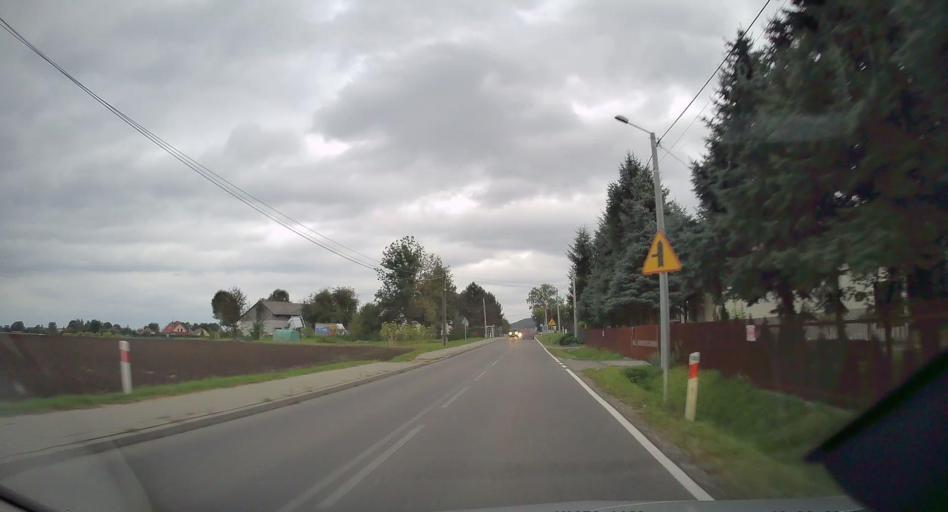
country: PL
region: Lesser Poland Voivodeship
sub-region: Powiat krakowski
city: Slomniki
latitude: 50.1945
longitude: 20.0910
